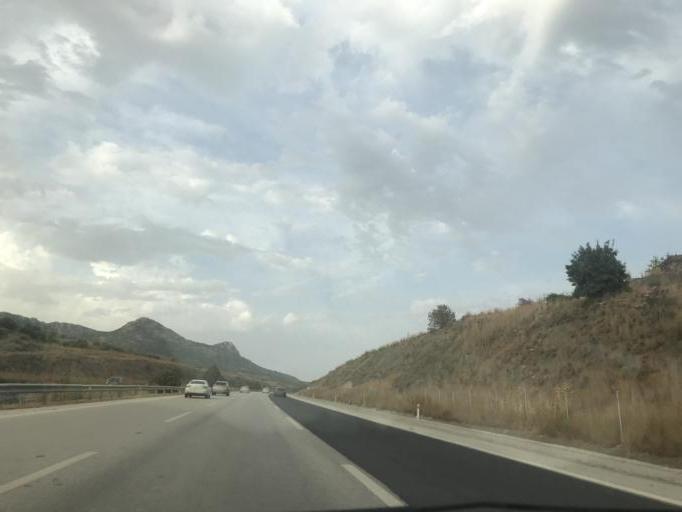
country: TR
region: Adana
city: Ceyhan
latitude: 37.0118
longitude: 35.9655
